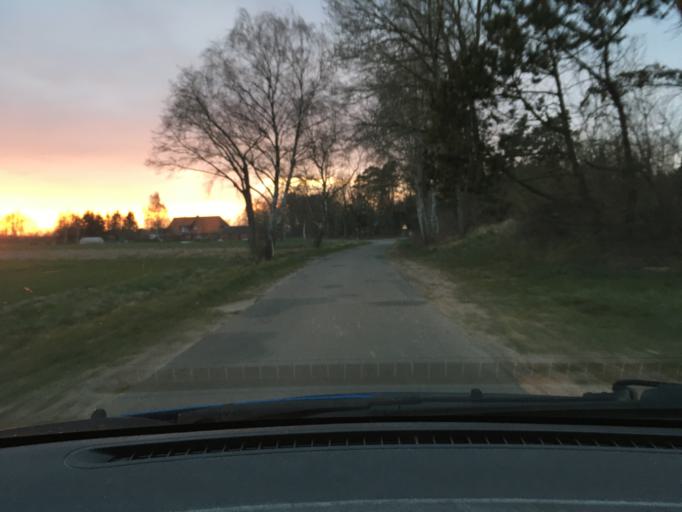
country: DE
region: Lower Saxony
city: Bleckede
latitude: 53.2951
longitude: 10.6844
